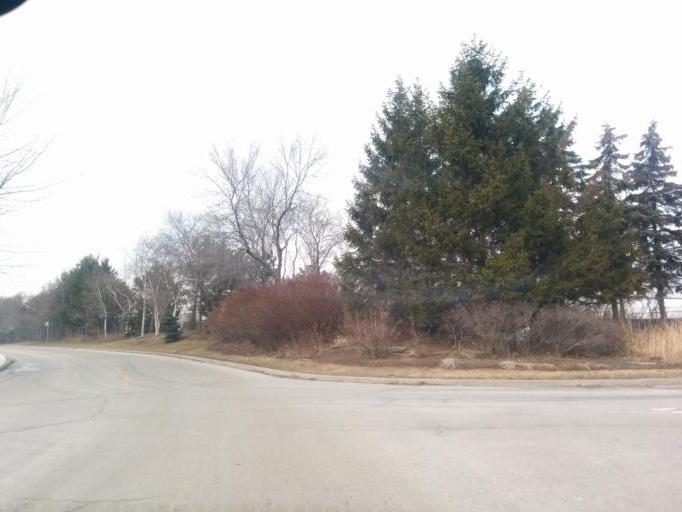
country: CA
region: Ontario
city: Etobicoke
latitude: 43.5646
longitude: -79.5591
